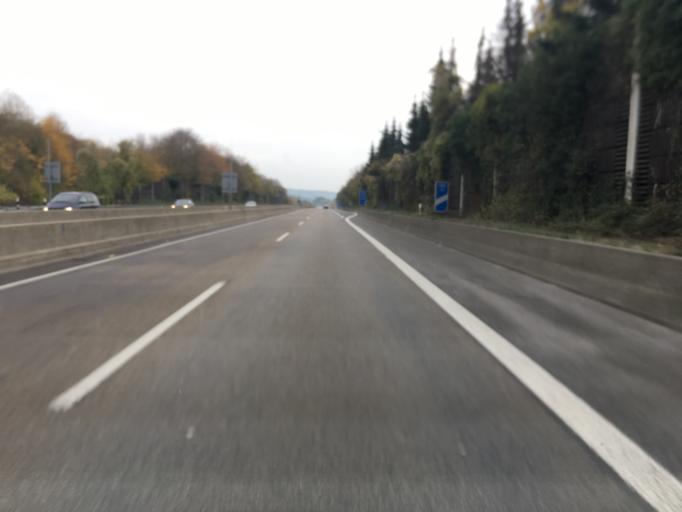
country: DE
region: North Rhine-Westphalia
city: Wulfrath
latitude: 51.2589
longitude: 7.0859
